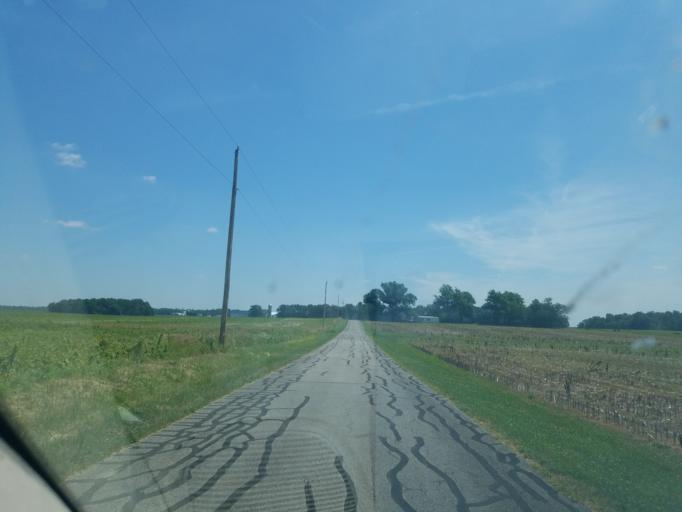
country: US
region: Ohio
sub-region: Hancock County
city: Arlington
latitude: 40.8631
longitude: -83.7164
